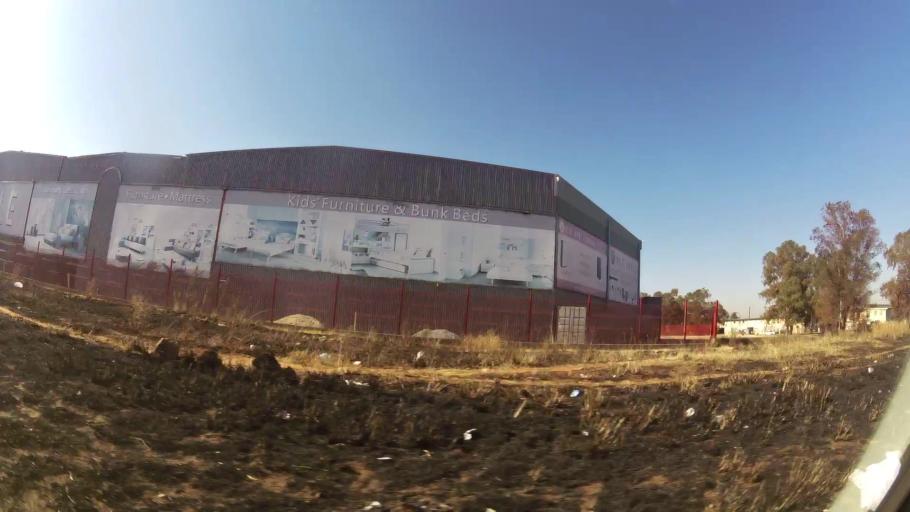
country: ZA
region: Gauteng
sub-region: City of Johannesburg Metropolitan Municipality
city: Johannesburg
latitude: -26.2305
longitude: 28.0897
